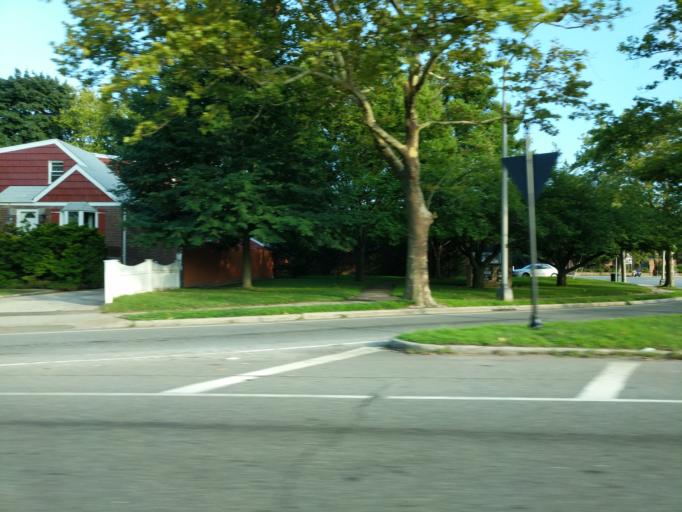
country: US
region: New York
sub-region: Nassau County
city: Hewlett
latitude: 40.6501
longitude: -73.6893
